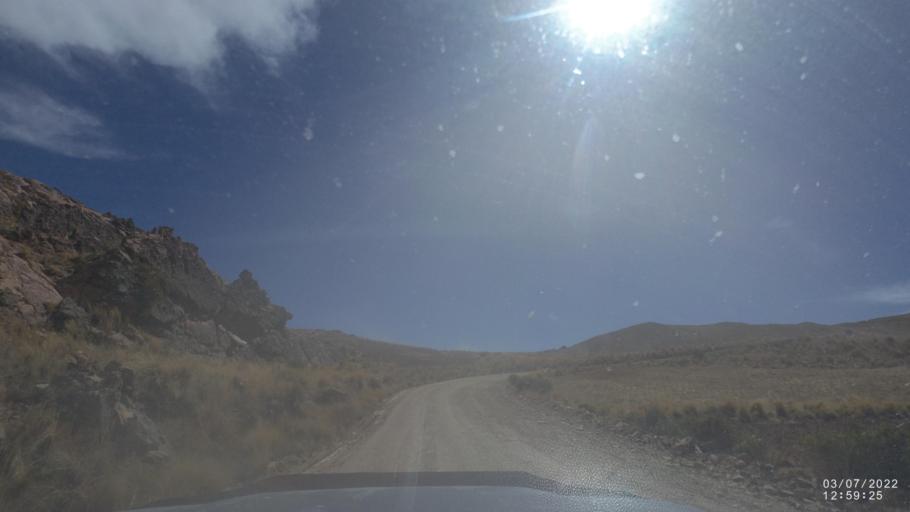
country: BO
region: Cochabamba
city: Colchani
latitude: -17.7163
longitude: -66.6852
